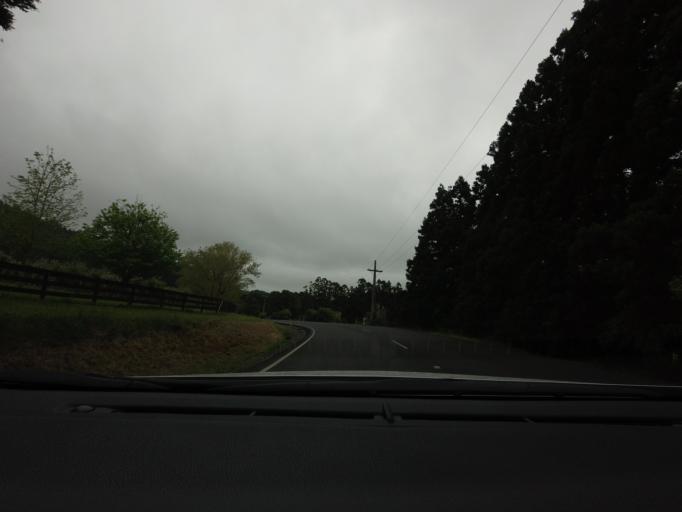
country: NZ
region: Auckland
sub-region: Auckland
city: Wellsford
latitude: -36.2831
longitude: 174.6096
